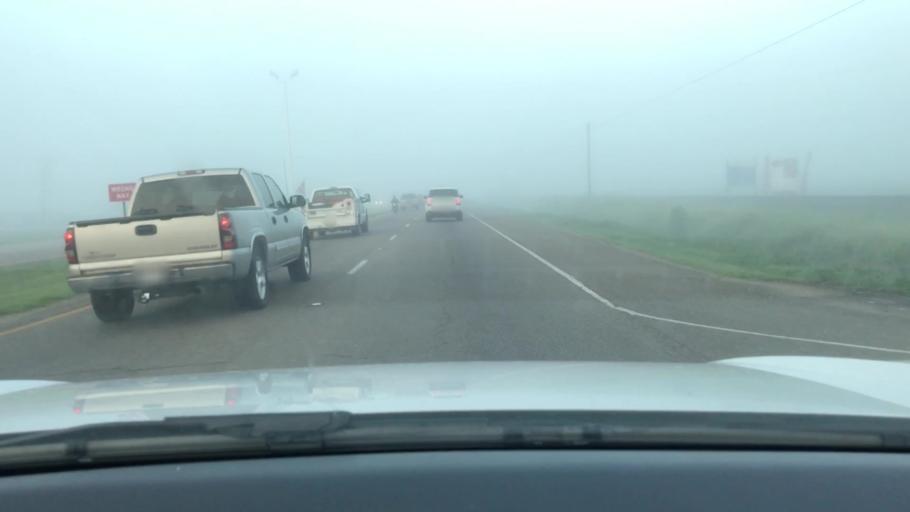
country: US
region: Louisiana
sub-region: West Baton Rouge Parish
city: Brusly
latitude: 30.3735
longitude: -91.2548
